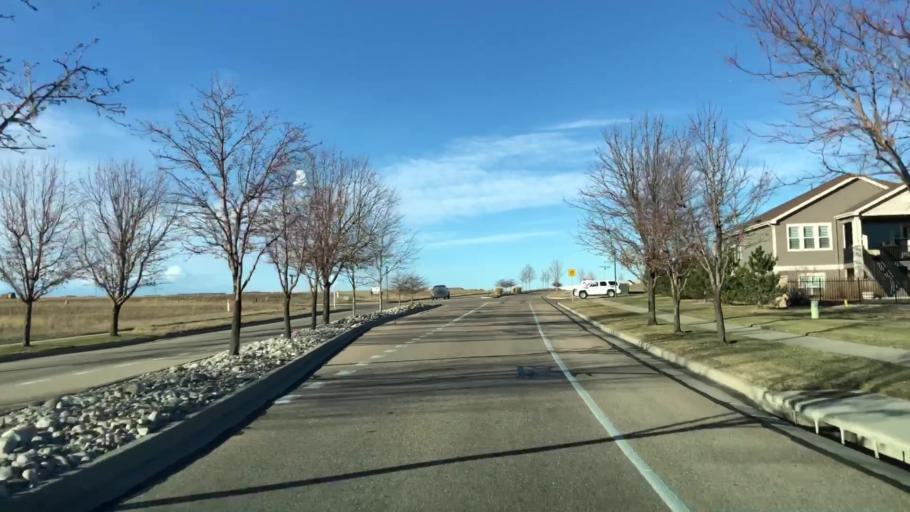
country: US
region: Colorado
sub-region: Weld County
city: Windsor
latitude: 40.4501
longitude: -104.9770
